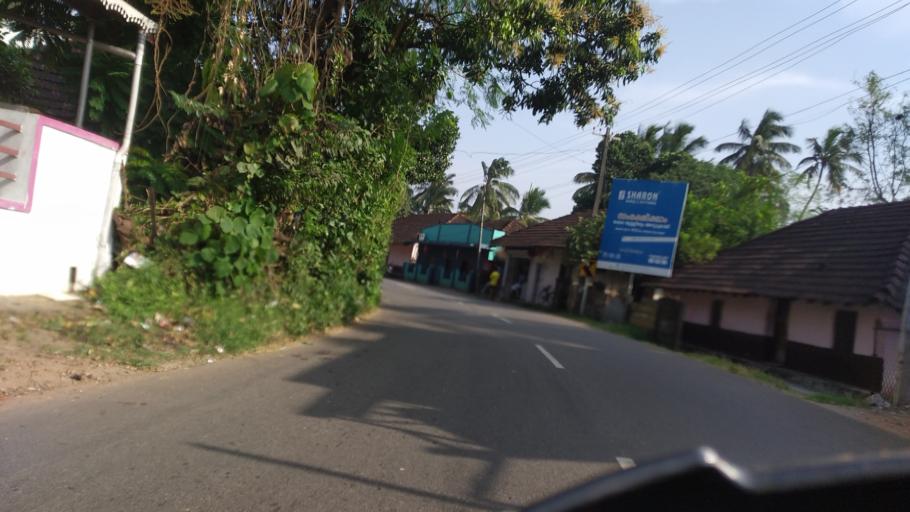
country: IN
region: Kerala
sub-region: Palakkad district
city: Palakkad
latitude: 10.6017
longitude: 76.5438
